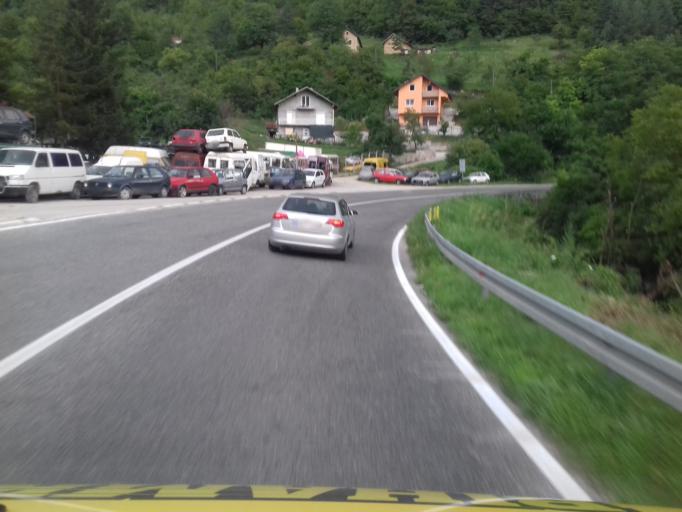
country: BA
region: Federation of Bosnia and Herzegovina
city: Konjic
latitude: 43.6873
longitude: 17.8716
